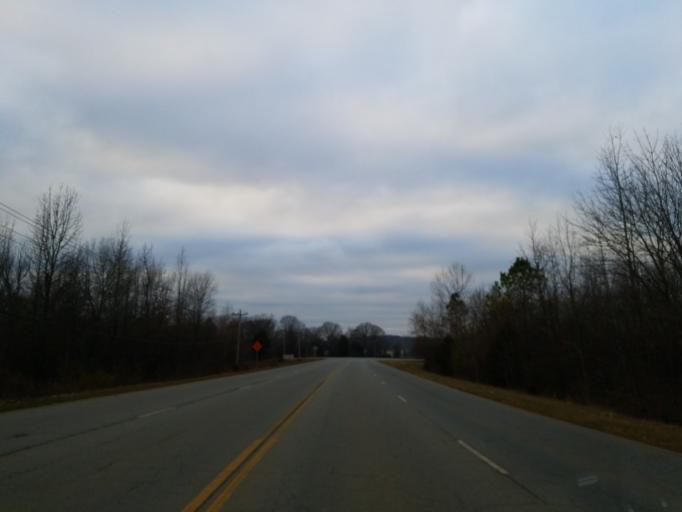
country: US
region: Georgia
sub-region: Gordon County
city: Calhoun
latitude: 34.4423
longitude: -84.9304
